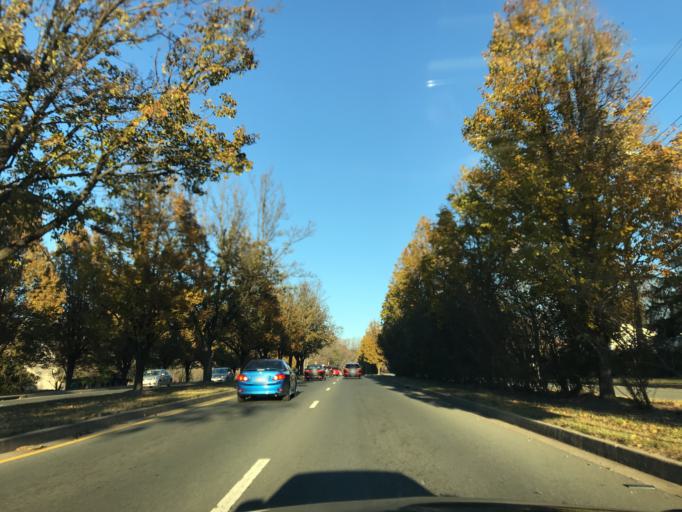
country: US
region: Maryland
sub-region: Montgomery County
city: Rossmoor
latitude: 39.1074
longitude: -77.0830
